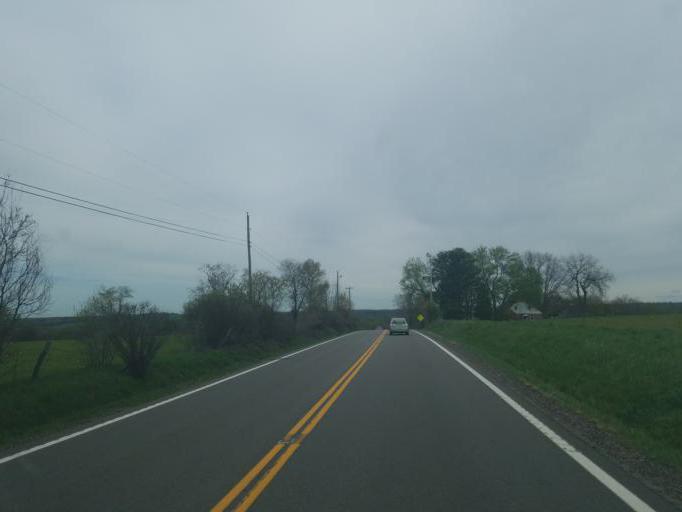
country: US
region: Ohio
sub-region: Wayne County
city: Rittman
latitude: 40.9373
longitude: -81.7496
